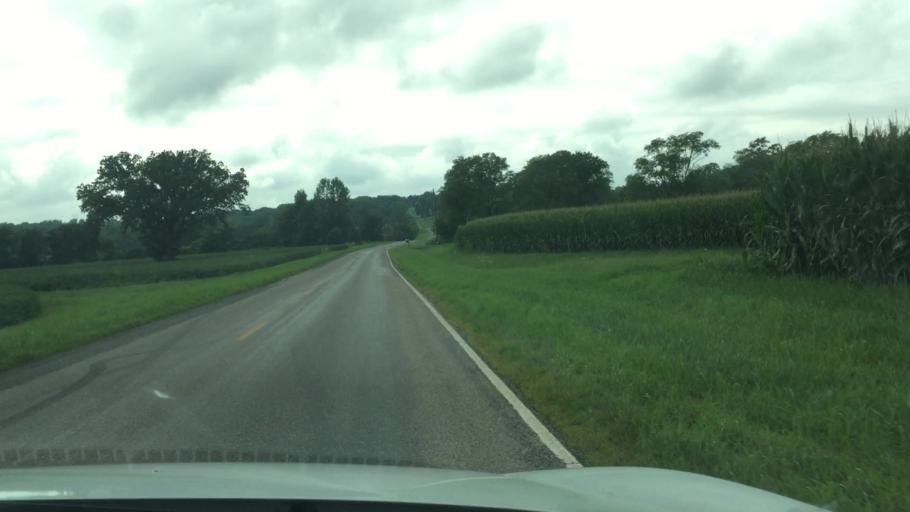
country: US
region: Ohio
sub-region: Champaign County
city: Mechanicsburg
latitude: 40.0593
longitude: -83.6240
